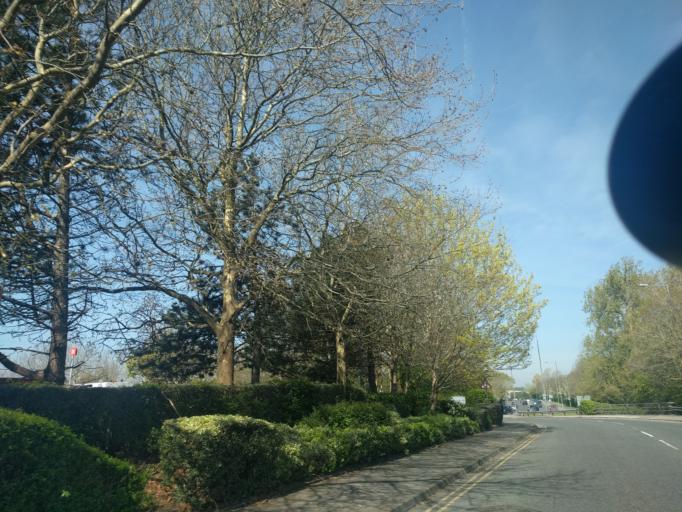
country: GB
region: England
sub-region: Borough of Swindon
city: Swindon
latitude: 51.5596
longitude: -1.8098
